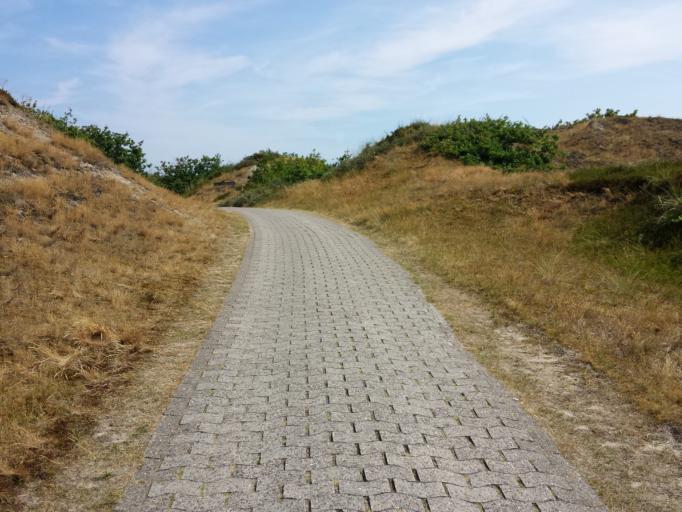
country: DE
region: Lower Saxony
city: Spiekeroog
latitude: 53.7744
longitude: 7.6963
